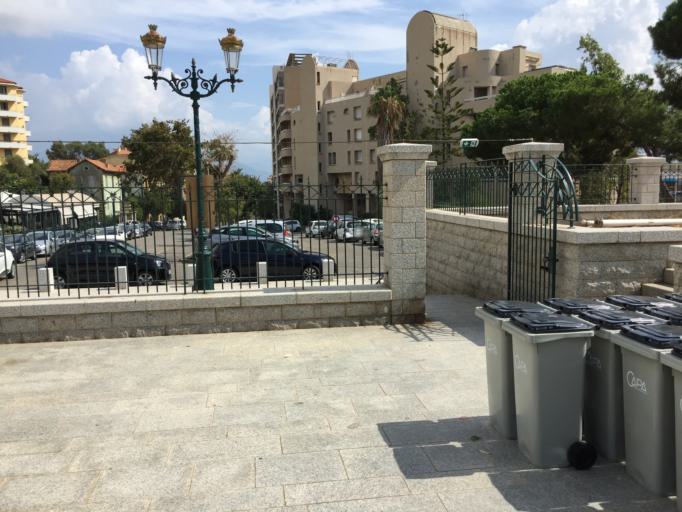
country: FR
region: Corsica
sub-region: Departement de la Corse-du-Sud
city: Ajaccio
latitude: 41.9167
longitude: 8.7253
